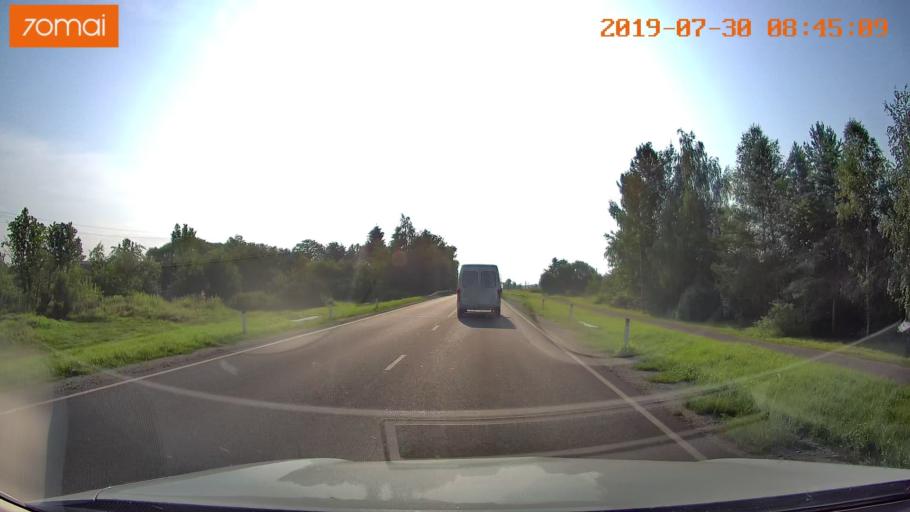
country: RU
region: Kaliningrad
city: Chernyakhovsk
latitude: 54.6266
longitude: 21.8631
